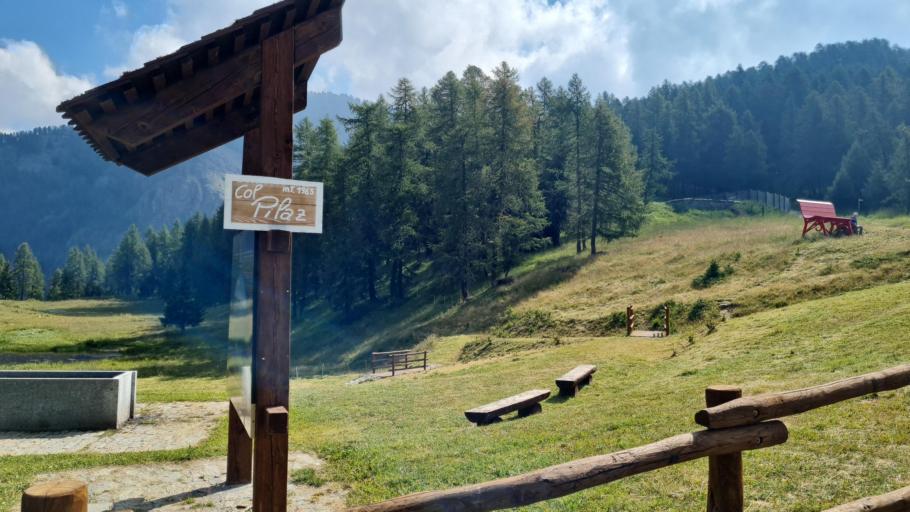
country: IT
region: Aosta Valley
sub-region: Valle d'Aosta
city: La Magdeleine
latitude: 45.8217
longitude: 7.6189
